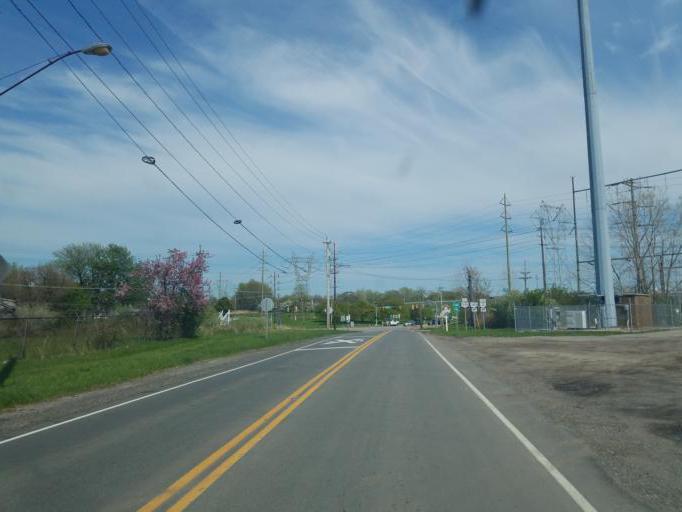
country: US
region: Ohio
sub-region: Lake County
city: Painesville
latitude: 41.7308
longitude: -81.2638
